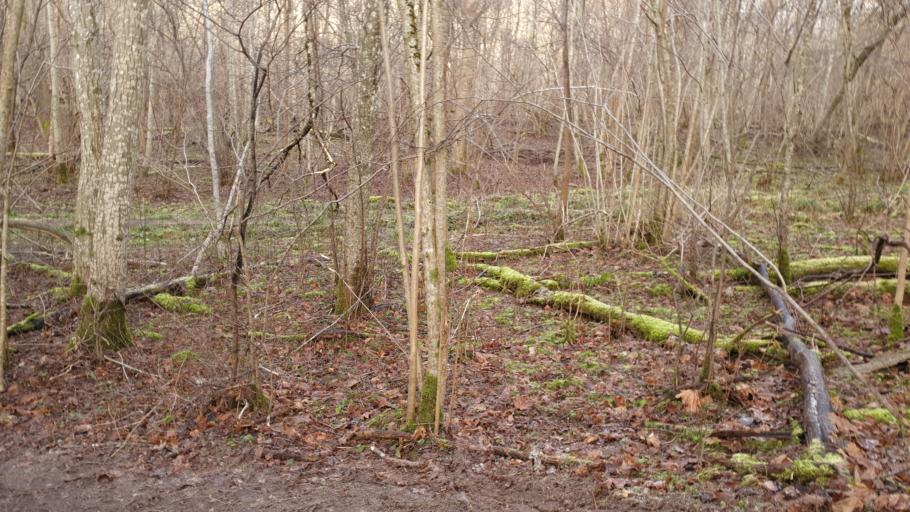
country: LT
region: Vilnius County
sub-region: Vilniaus Rajonas
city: Vievis
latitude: 54.8199
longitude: 24.9359
